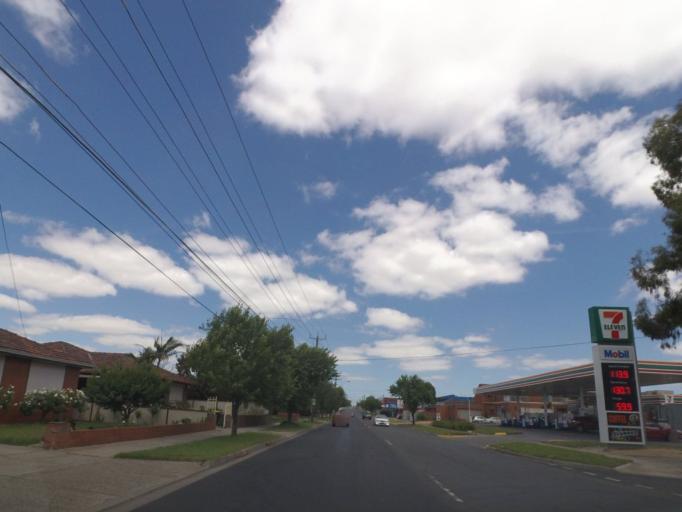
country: AU
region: Victoria
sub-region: Whittlesea
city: Lalor
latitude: -37.6603
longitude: 145.0248
